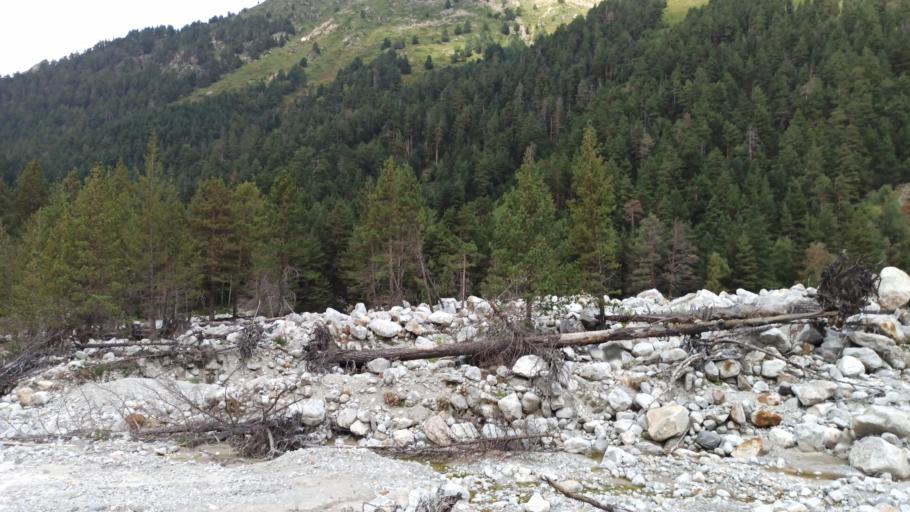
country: RU
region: Kabardino-Balkariya
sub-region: El'brusskiy Rayon
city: El'brus
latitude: 43.2174
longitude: 42.6960
